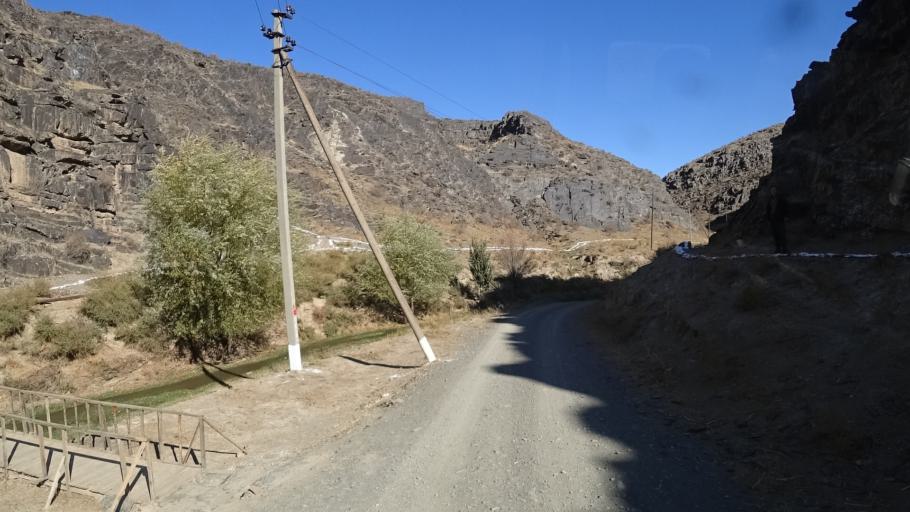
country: UZ
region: Navoiy
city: Nurota
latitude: 40.3058
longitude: 65.6175
